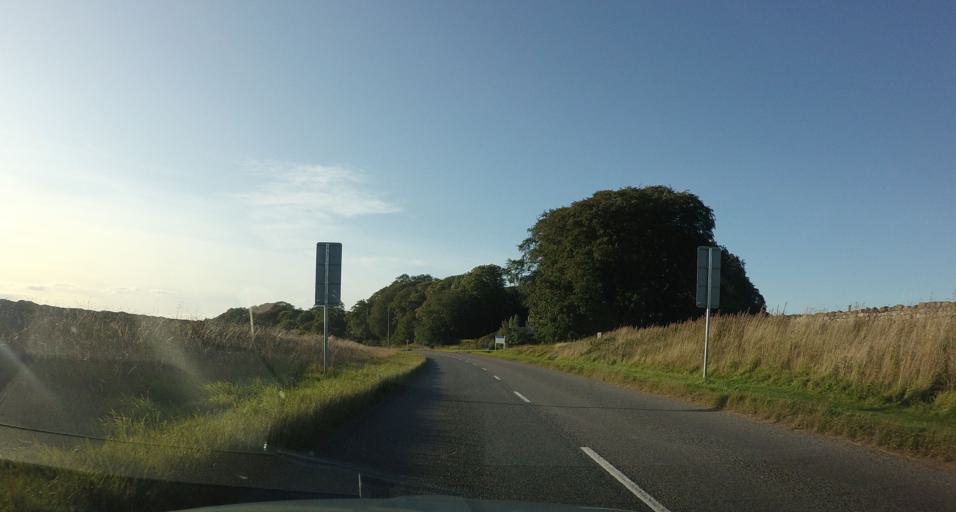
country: GB
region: Scotland
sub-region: Aberdeenshire
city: Westhill
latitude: 57.1539
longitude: -2.3200
